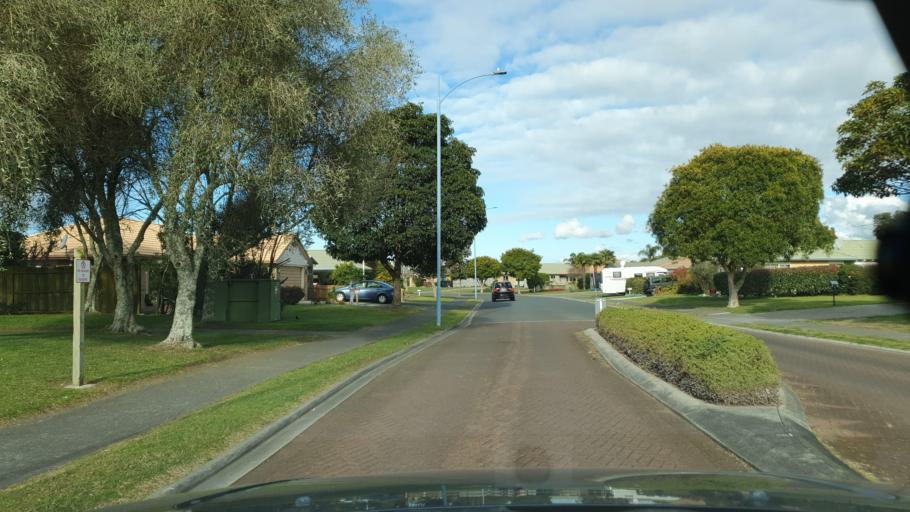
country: NZ
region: Bay of Plenty
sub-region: Tauranga City
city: Tauranga
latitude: -37.7082
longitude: 176.2858
